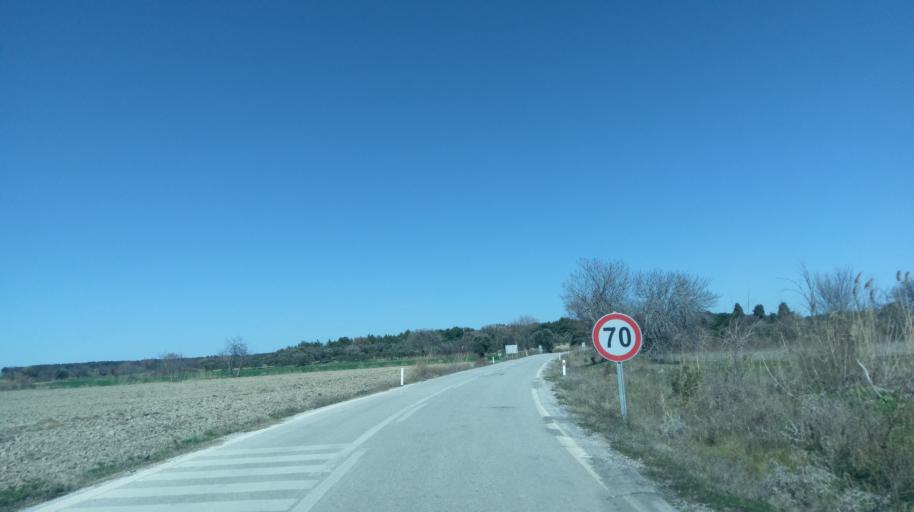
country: TR
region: Canakkale
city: Intepe
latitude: 40.0562
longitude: 26.1968
